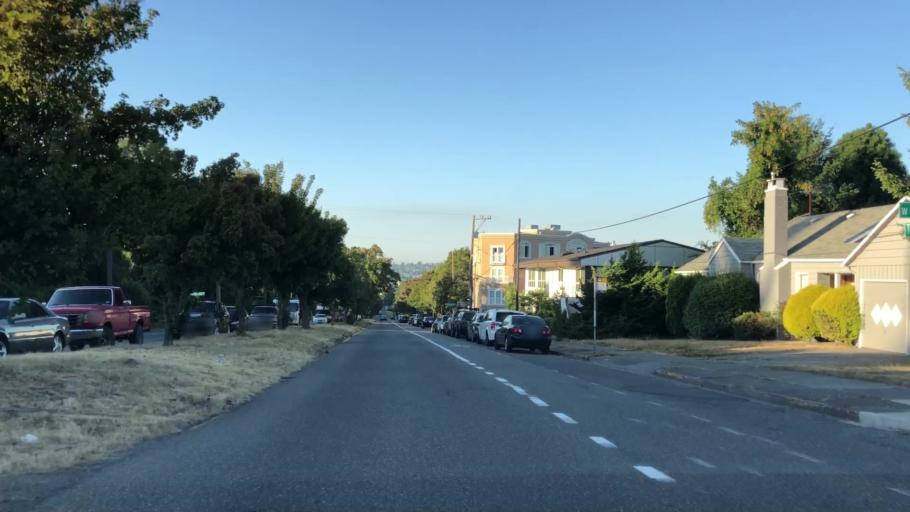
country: US
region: Washington
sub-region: King County
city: Seattle
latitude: 47.6370
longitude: -122.3889
